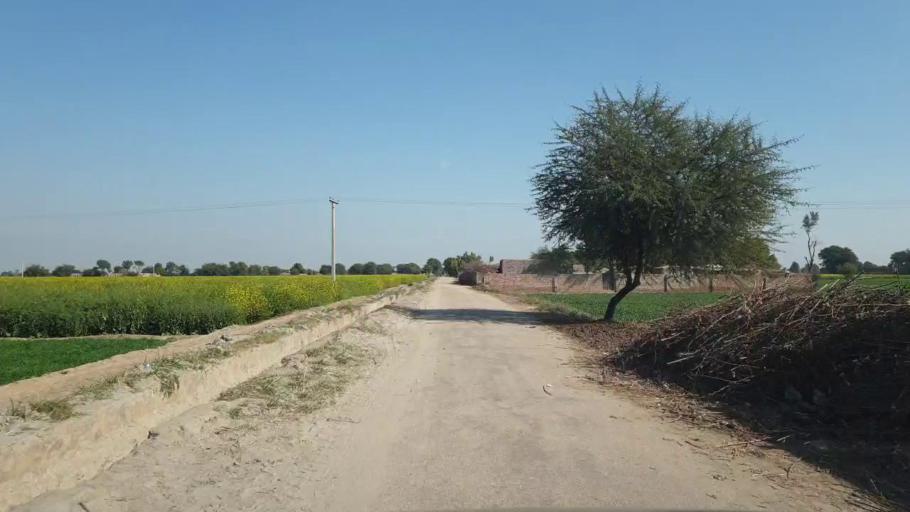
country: PK
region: Sindh
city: Shahpur Chakar
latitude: 26.1080
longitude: 68.6506
